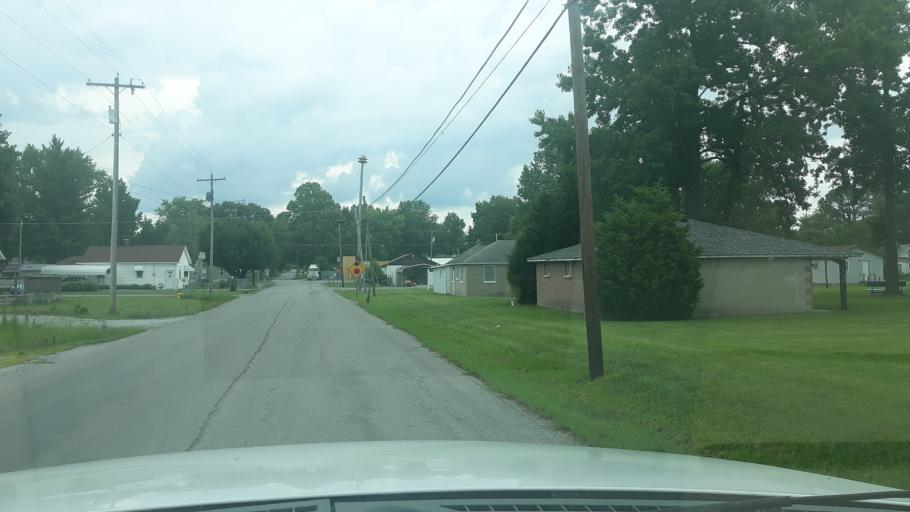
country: US
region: Illinois
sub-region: Saline County
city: Eldorado
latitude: 37.8060
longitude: -88.4566
